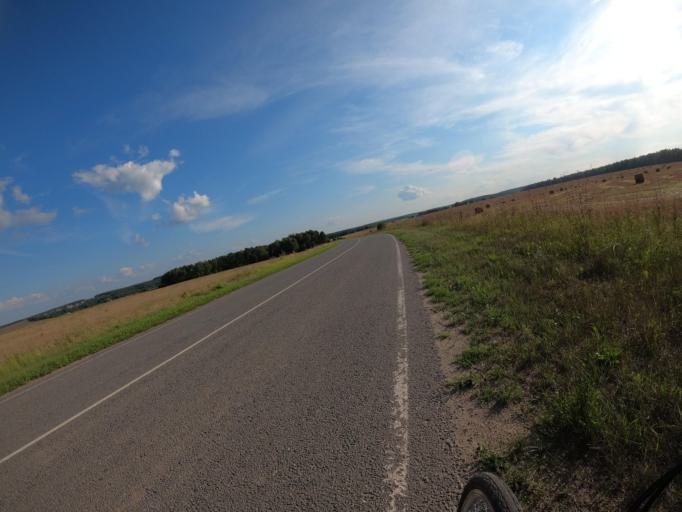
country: RU
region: Moskovskaya
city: Meshcherino
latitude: 55.1581
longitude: 38.4336
